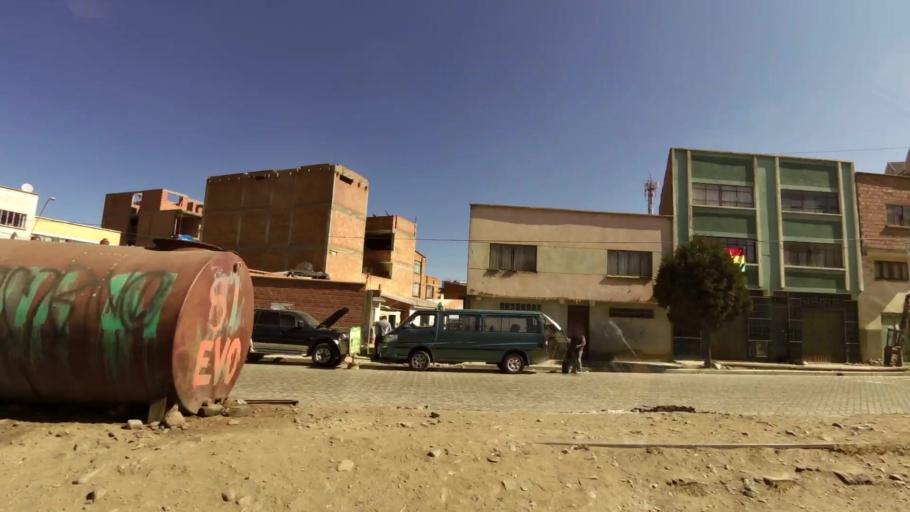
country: BO
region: La Paz
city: La Paz
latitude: -16.5168
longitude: -68.1565
